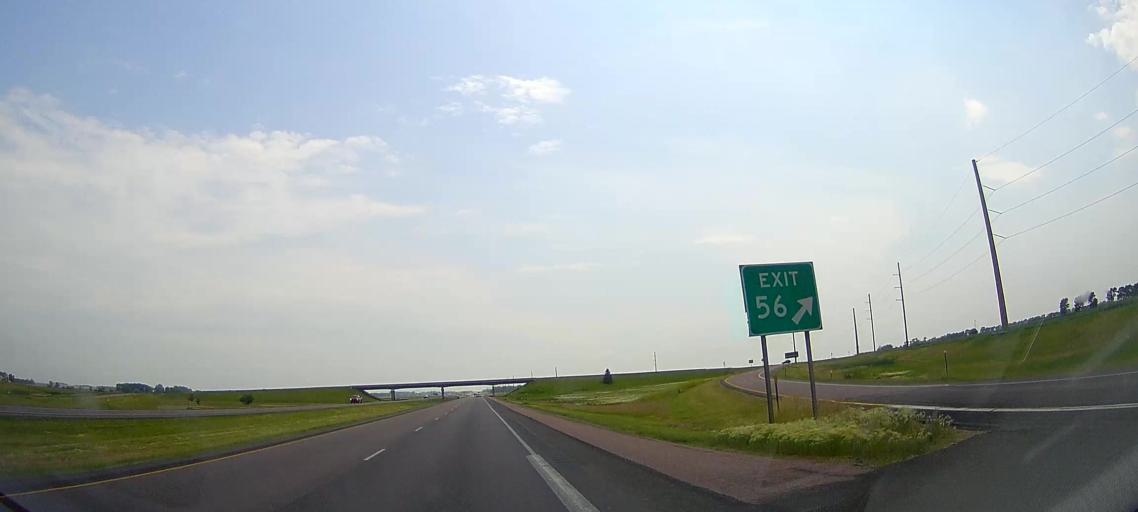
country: US
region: South Dakota
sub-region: Union County
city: Beresford
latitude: 43.2165
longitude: -96.7962
